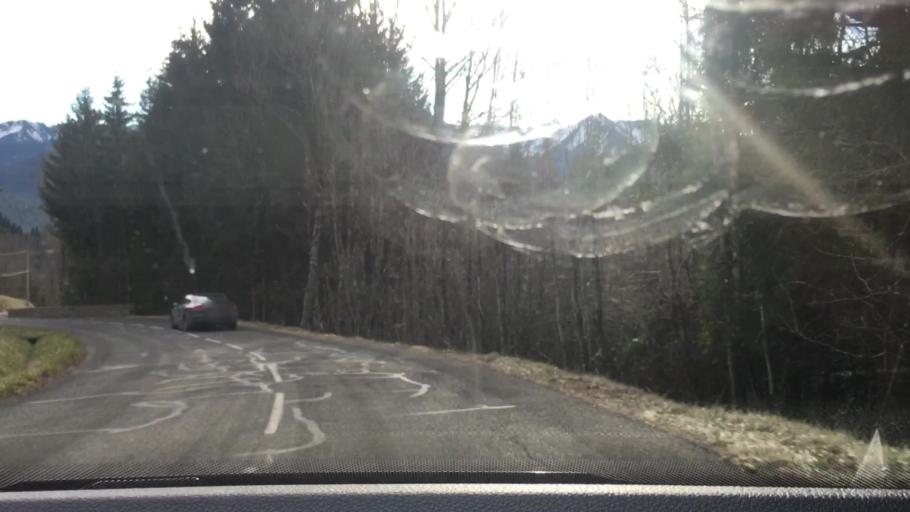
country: FR
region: Rhone-Alpes
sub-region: Departement de la Haute-Savoie
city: Abondance
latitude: 46.2793
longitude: 6.6312
